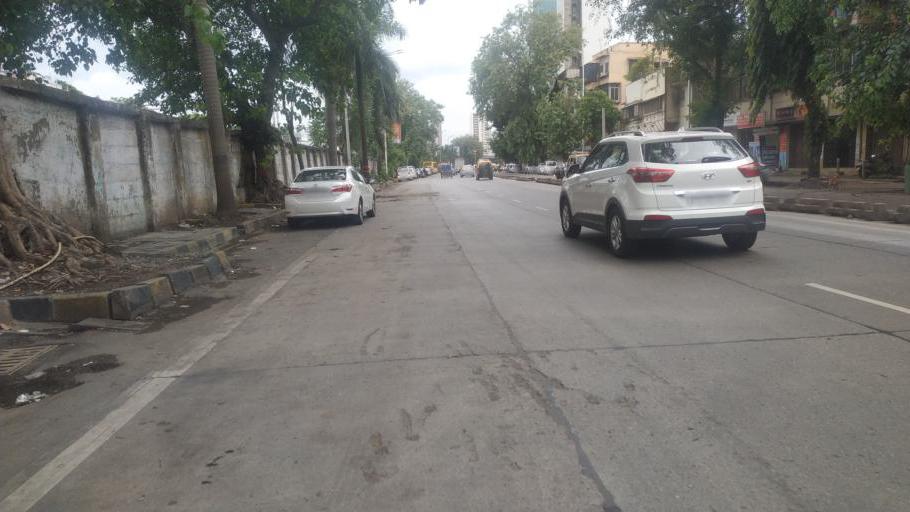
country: IN
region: Maharashtra
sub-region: Mumbai Suburban
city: Mumbai
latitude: 19.0341
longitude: 72.8478
